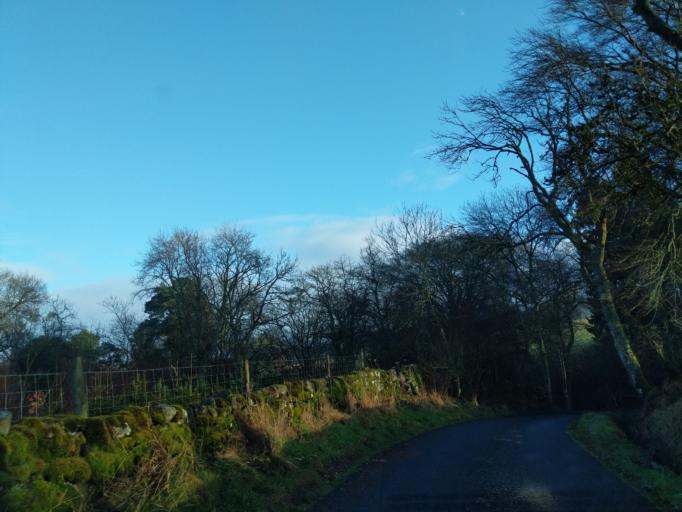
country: GB
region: Scotland
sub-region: Perth and Kinross
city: Auchterarder
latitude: 56.2729
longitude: -3.7066
